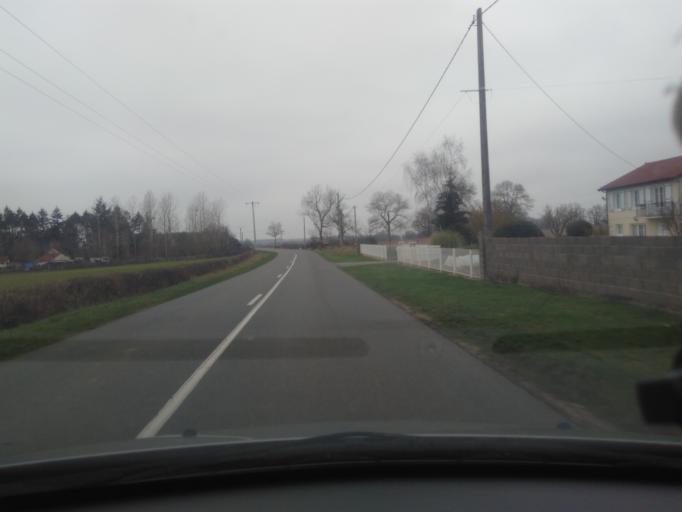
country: FR
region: Centre
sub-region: Departement du Cher
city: Le Chatelet
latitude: 46.6420
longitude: 2.3155
